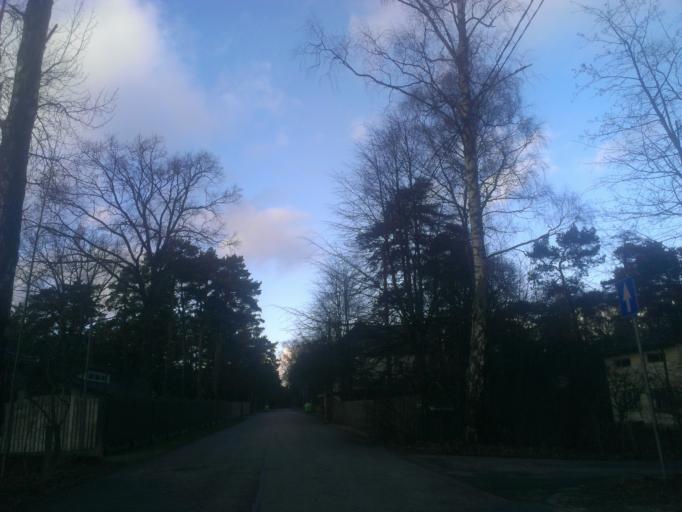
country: LV
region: Riga
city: Jaunciems
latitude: 57.0753
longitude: 24.1140
